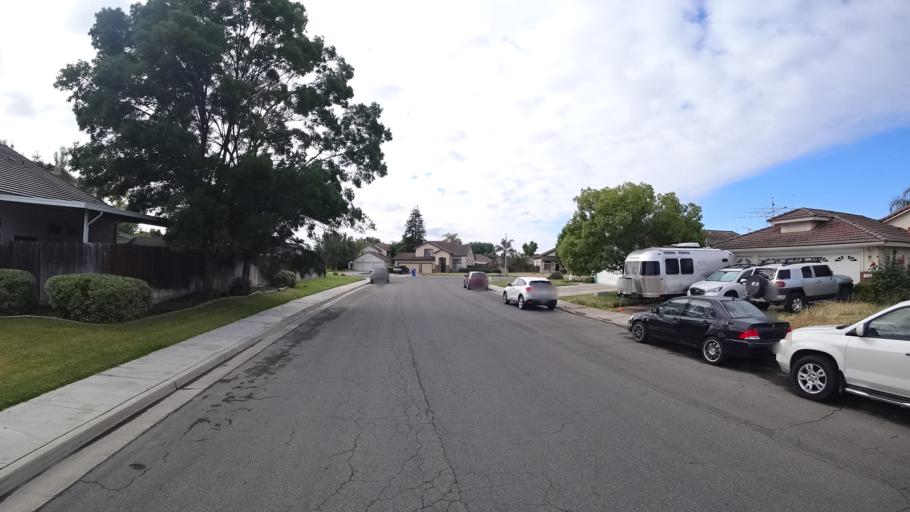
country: US
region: California
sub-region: Kings County
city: Lucerne
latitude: 36.3629
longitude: -119.6329
